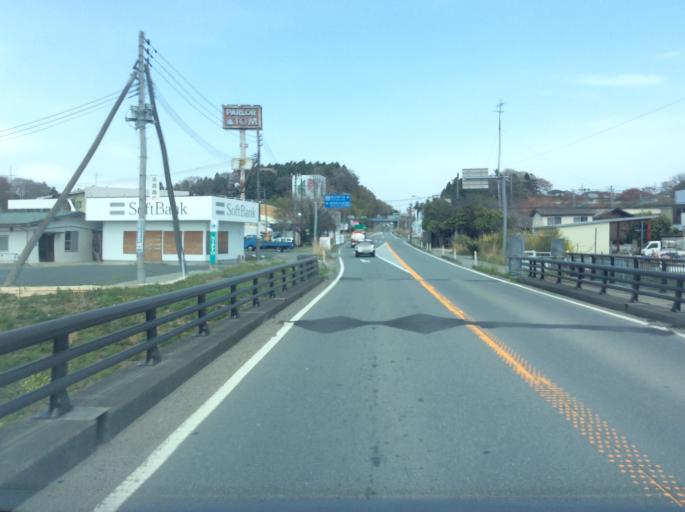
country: JP
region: Fukushima
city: Namie
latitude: 37.3419
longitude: 141.0130
